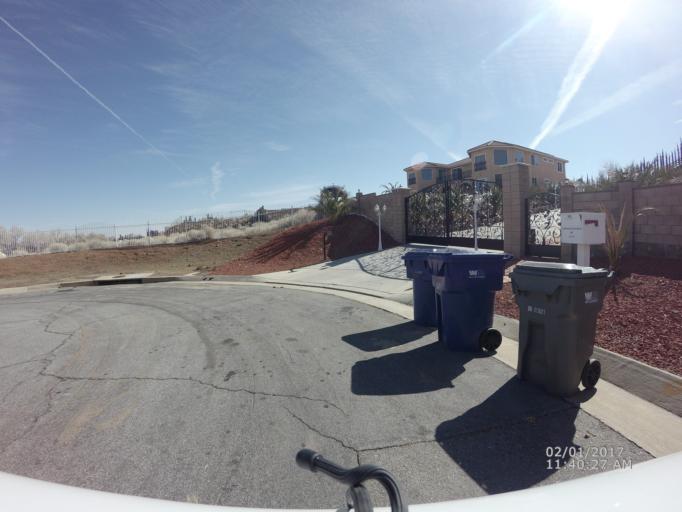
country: US
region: California
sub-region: Los Angeles County
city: Palmdale
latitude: 34.5458
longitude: -118.1216
